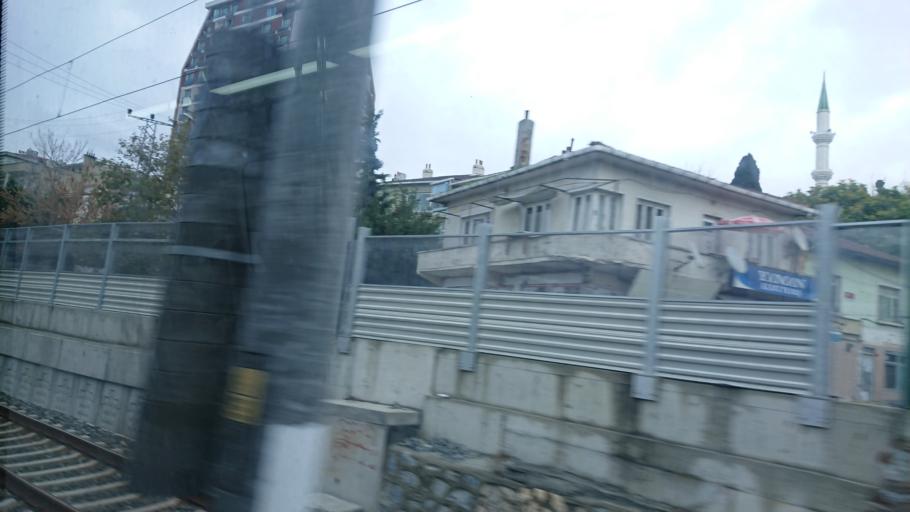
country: TR
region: Istanbul
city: Mahmutbey
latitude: 40.9915
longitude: 28.7717
